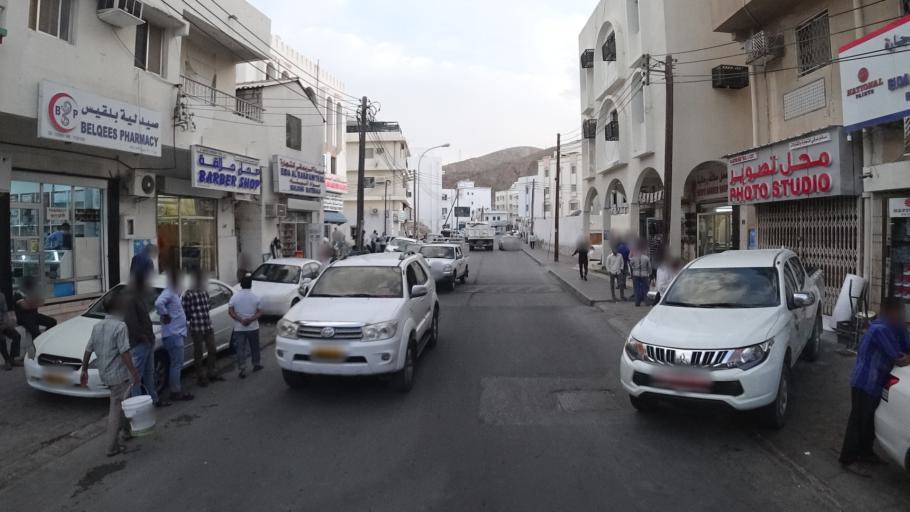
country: OM
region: Muhafazat Masqat
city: Muscat
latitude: 23.5820
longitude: 58.5456
